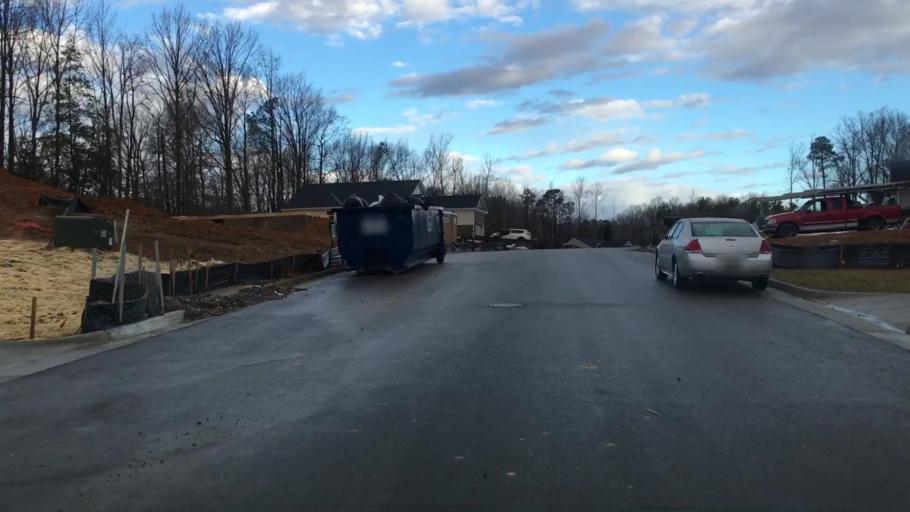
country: US
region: Virginia
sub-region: Chesterfield County
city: Bon Air
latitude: 37.4775
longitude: -77.5900
